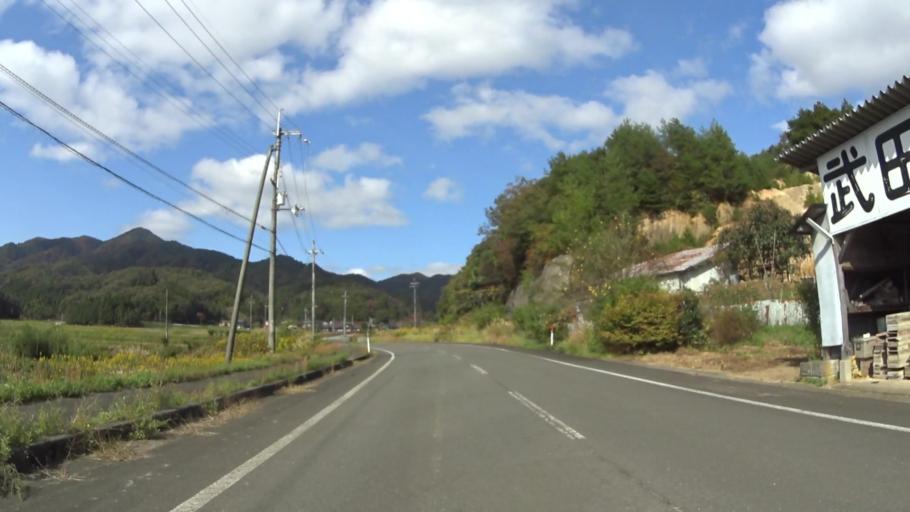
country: JP
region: Hyogo
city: Toyooka
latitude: 35.5032
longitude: 134.9925
